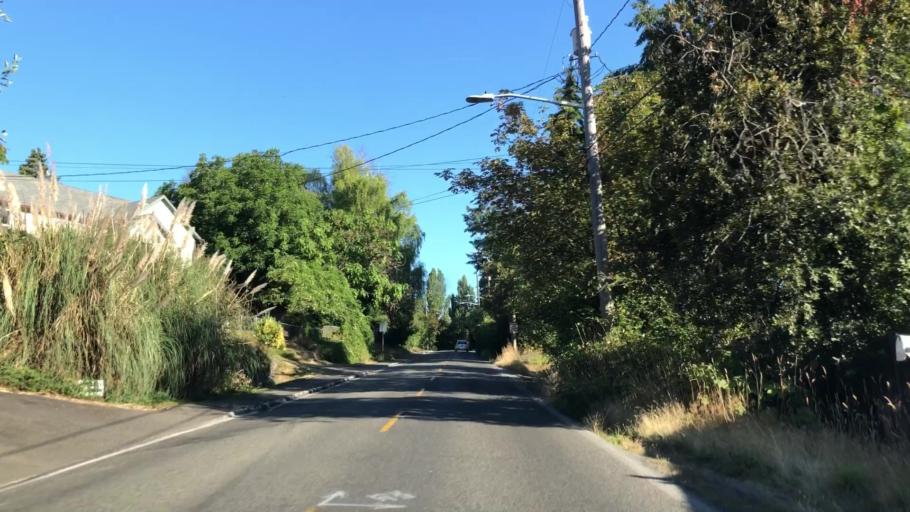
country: US
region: Washington
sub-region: King County
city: White Center
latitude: 47.5561
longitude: -122.3590
